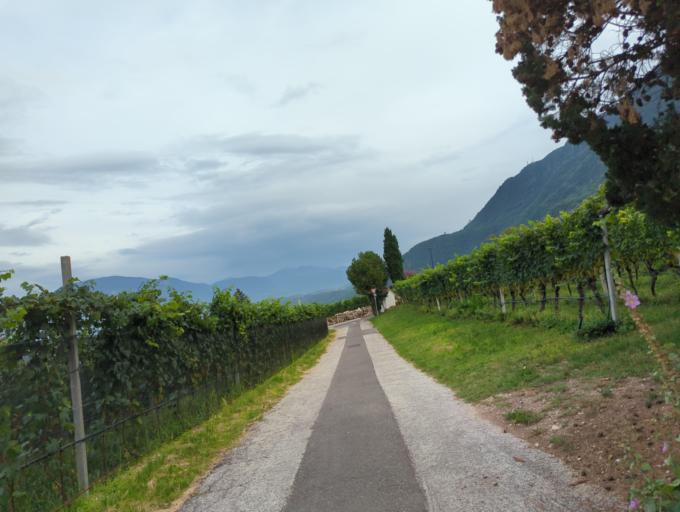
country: IT
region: Trentino-Alto Adige
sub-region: Bolzano
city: Andriano
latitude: 46.5175
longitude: 11.2292
